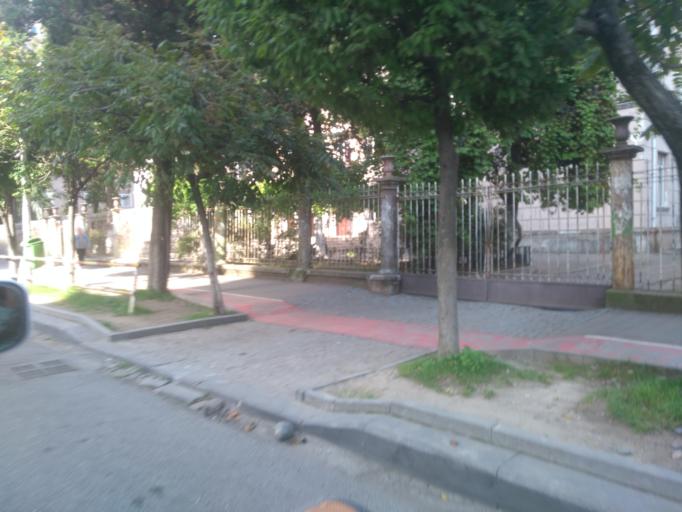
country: GE
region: Ajaria
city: Batumi
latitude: 41.6417
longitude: 41.6243
